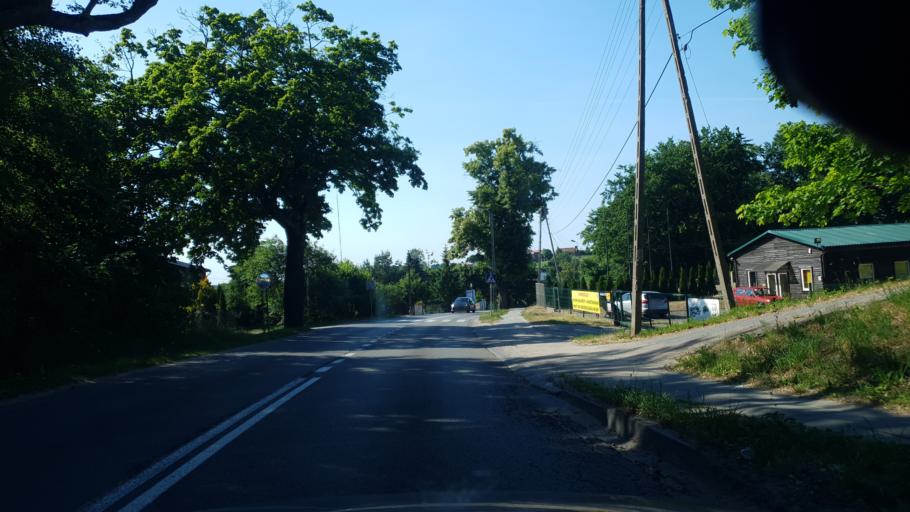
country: PL
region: Pomeranian Voivodeship
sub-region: Gdynia
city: Wielki Kack
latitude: 54.4361
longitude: 18.4638
